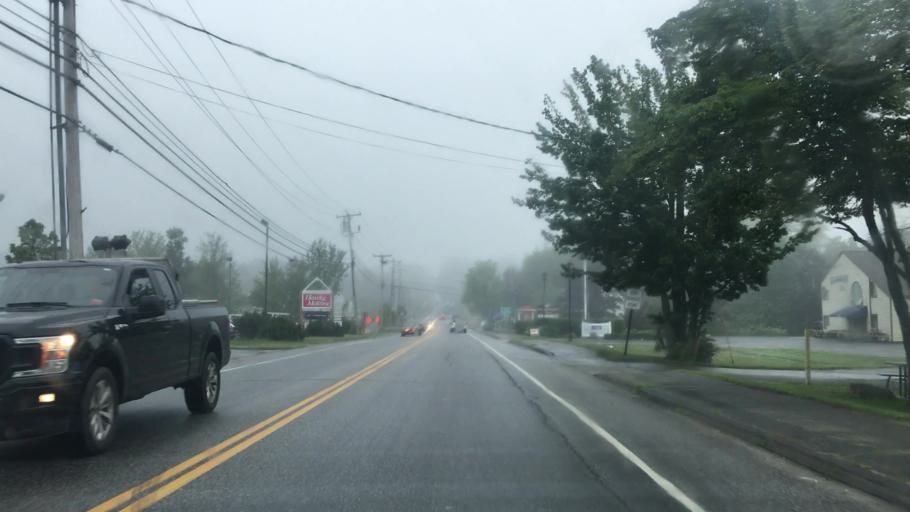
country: US
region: Maine
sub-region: Lincoln County
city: Boothbay Harbor
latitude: 43.8625
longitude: -69.6275
